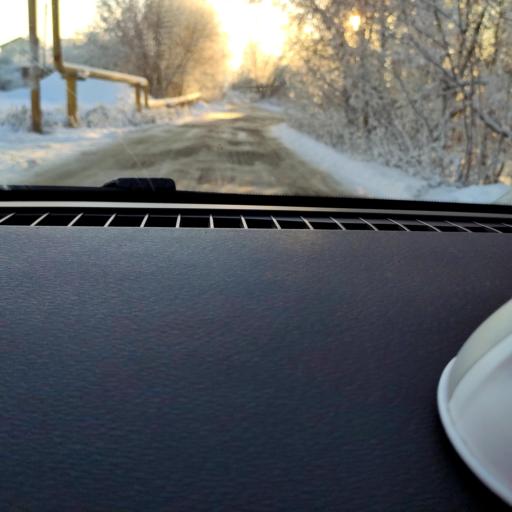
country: RU
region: Samara
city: Samara
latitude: 53.2710
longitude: 50.2296
